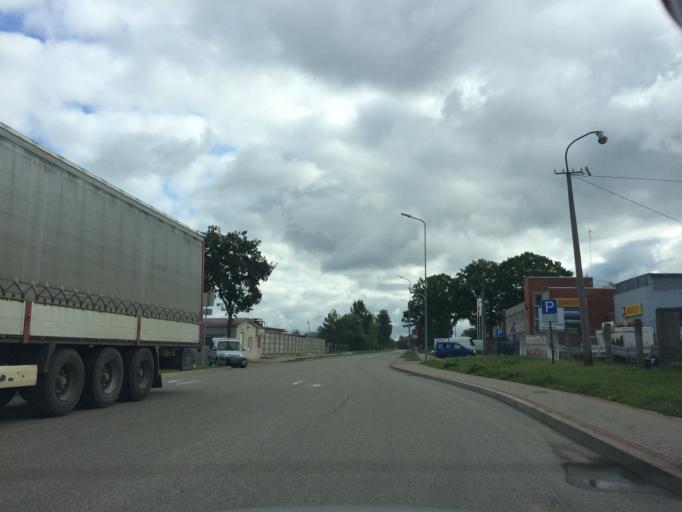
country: LV
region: Rezekne
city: Rezekne
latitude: 56.5135
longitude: 27.3244
